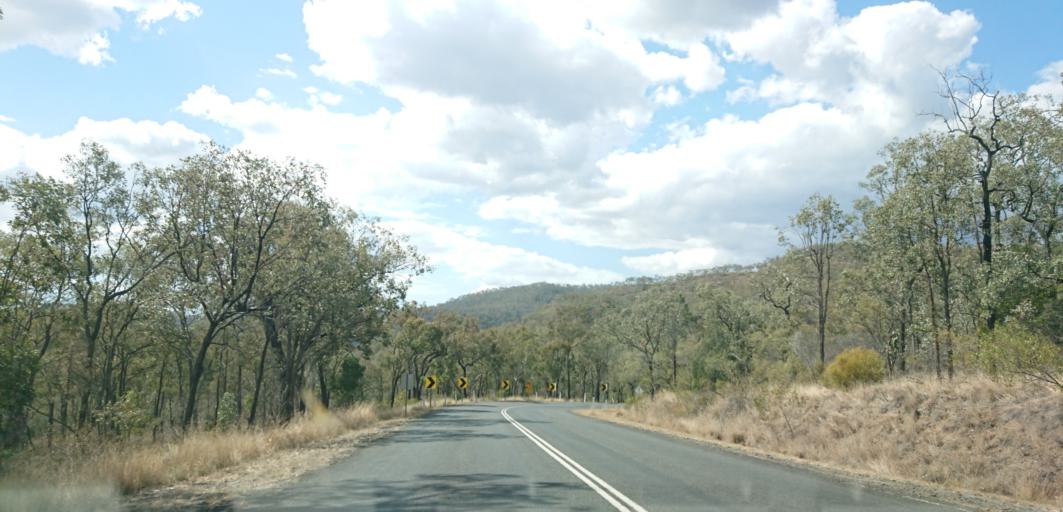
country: AU
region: Queensland
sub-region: Toowoomba
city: Top Camp
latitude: -27.8167
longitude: 152.1053
